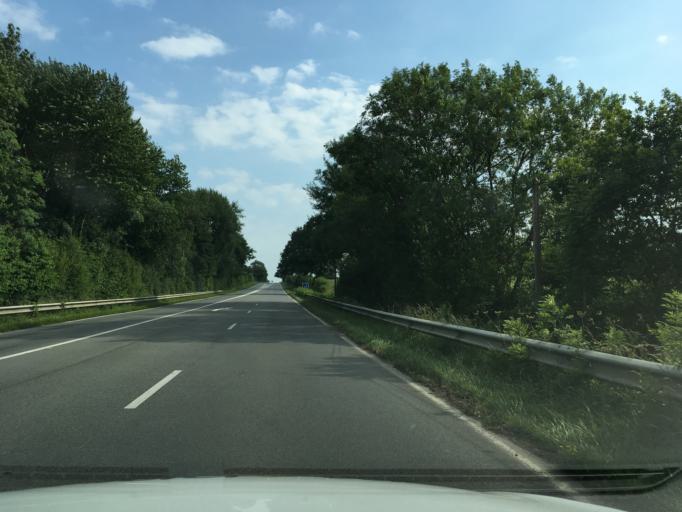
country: FR
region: Poitou-Charentes
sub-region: Departement des Deux-Sevres
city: Le Tallud
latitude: 46.6028
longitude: -0.2876
